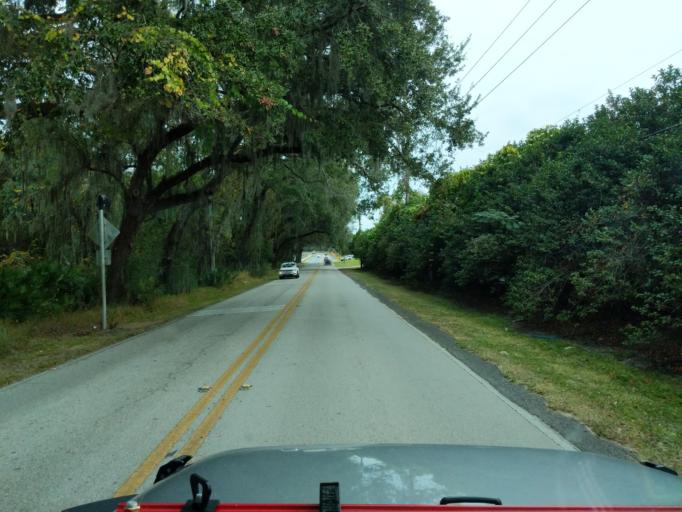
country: US
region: Florida
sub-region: Orange County
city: Oakland
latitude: 28.5279
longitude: -81.6114
